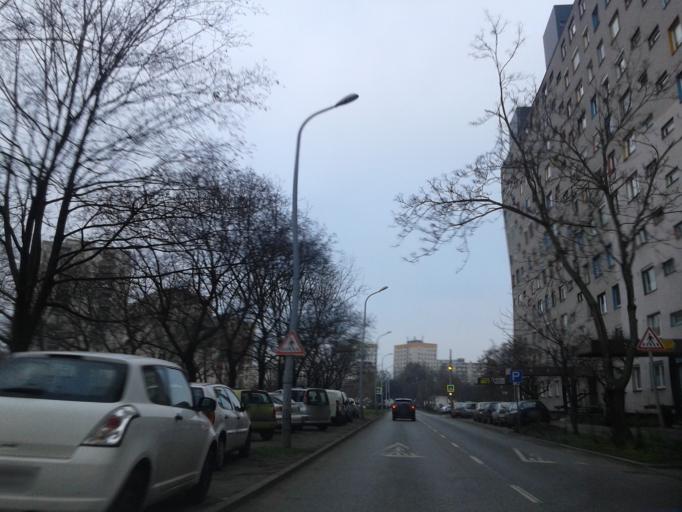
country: HU
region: Budapest
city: Budapest XV. keruelet
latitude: 47.5392
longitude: 19.1377
